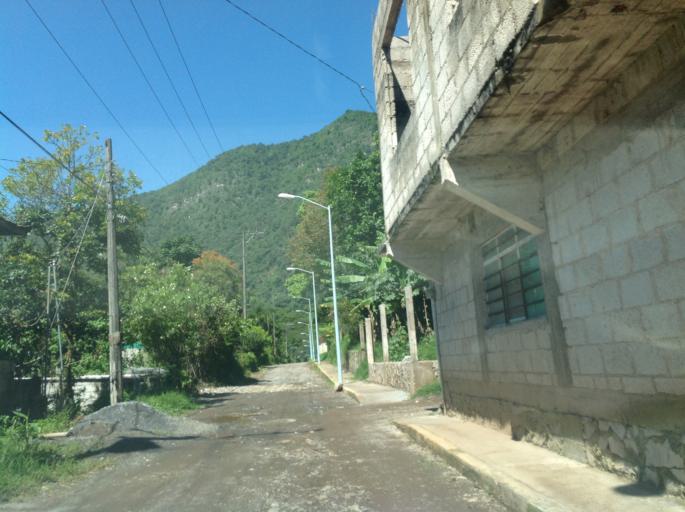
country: MX
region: Veracruz
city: Nogales
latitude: 18.8438
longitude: -97.1588
